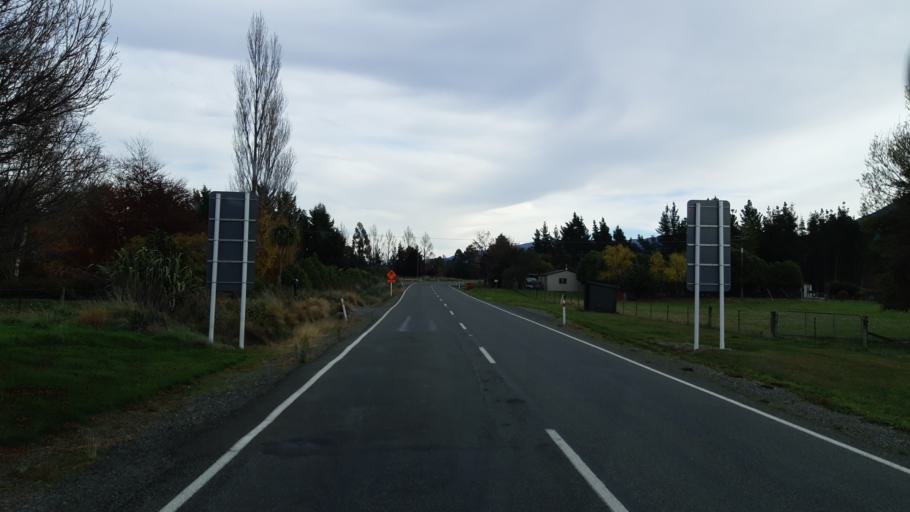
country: NZ
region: Tasman
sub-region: Tasman District
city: Brightwater
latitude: -41.6374
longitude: 173.3201
